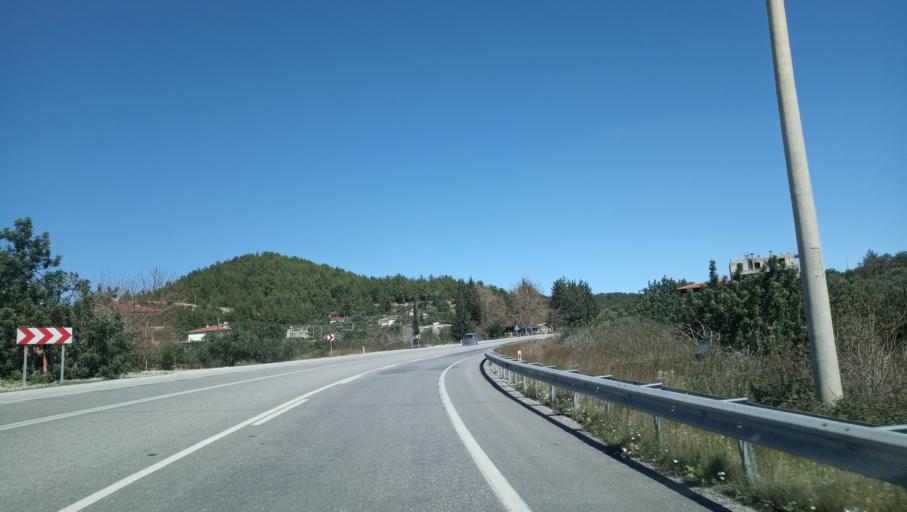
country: TR
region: Antalya
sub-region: Manavgat
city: Kizilagac
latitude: 36.7582
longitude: 31.6350
